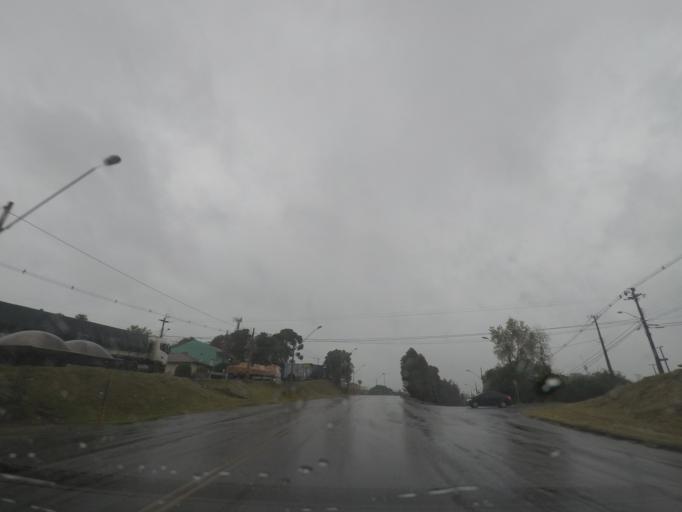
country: BR
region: Parana
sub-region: Almirante Tamandare
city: Almirante Tamandare
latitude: -25.3674
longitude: -49.2759
